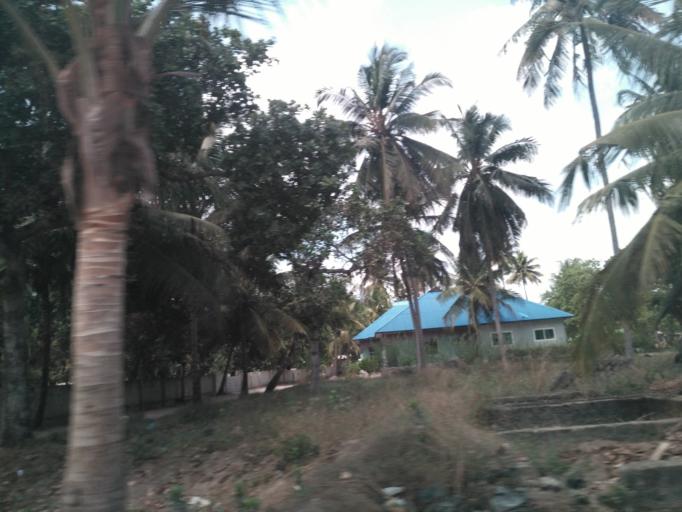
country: TZ
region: Dar es Salaam
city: Dar es Salaam
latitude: -6.8796
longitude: 39.3407
